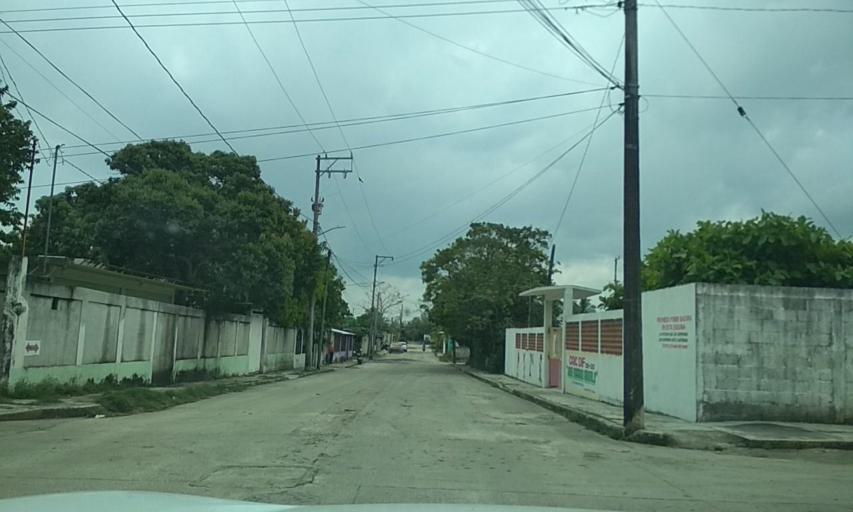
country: MX
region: Veracruz
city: Las Choapas
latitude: 17.8954
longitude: -94.0982
